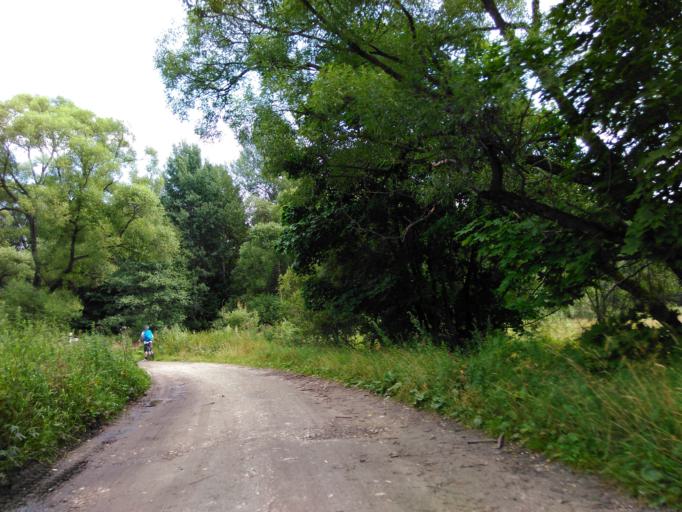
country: RU
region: Vladimir
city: Krasnyy Oktyabr'
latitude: 55.9981
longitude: 38.8618
